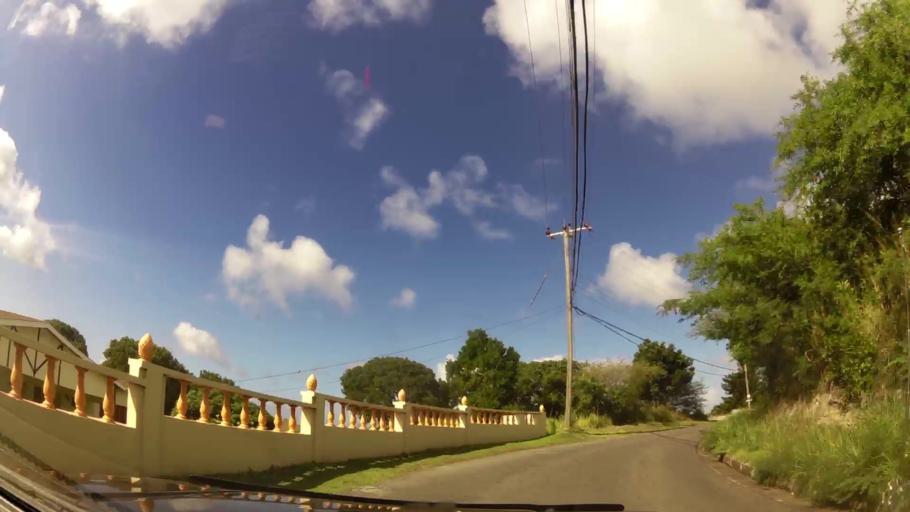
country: MS
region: Saint Peter
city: Saint Peters
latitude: 16.7537
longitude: -62.2225
